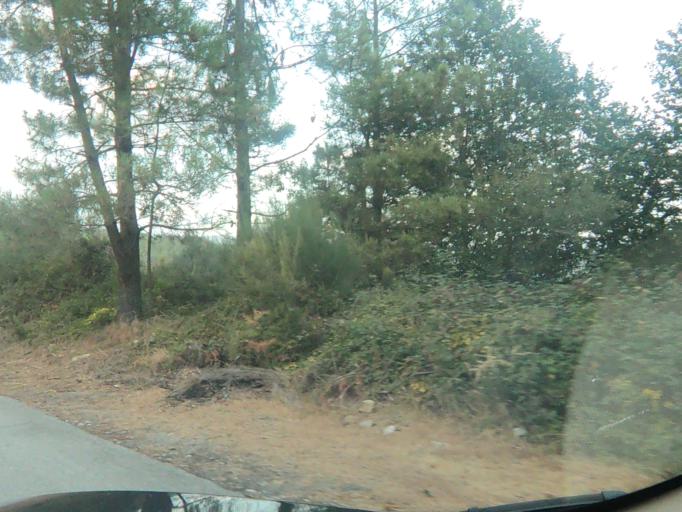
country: PT
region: Vila Real
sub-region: Santa Marta de Penaguiao
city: Santa Marta de Penaguiao
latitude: 41.2382
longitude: -7.8502
